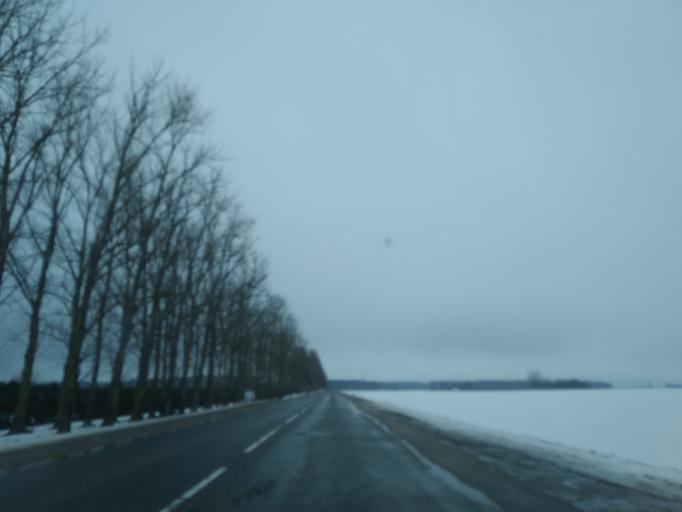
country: BY
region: Minsk
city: Stowbtsy
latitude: 53.5627
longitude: 26.7639
